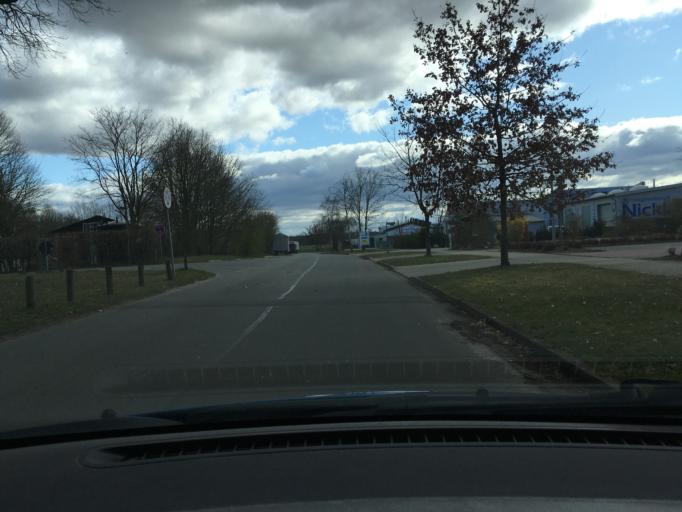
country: DE
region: Lower Saxony
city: Reppenstedt
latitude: 53.2459
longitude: 10.3527
